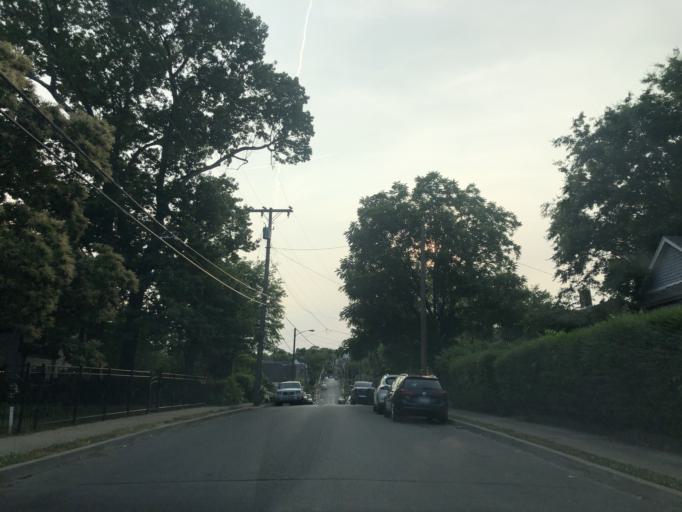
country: US
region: Tennessee
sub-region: Davidson County
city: Nashville
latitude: 36.1288
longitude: -86.7844
